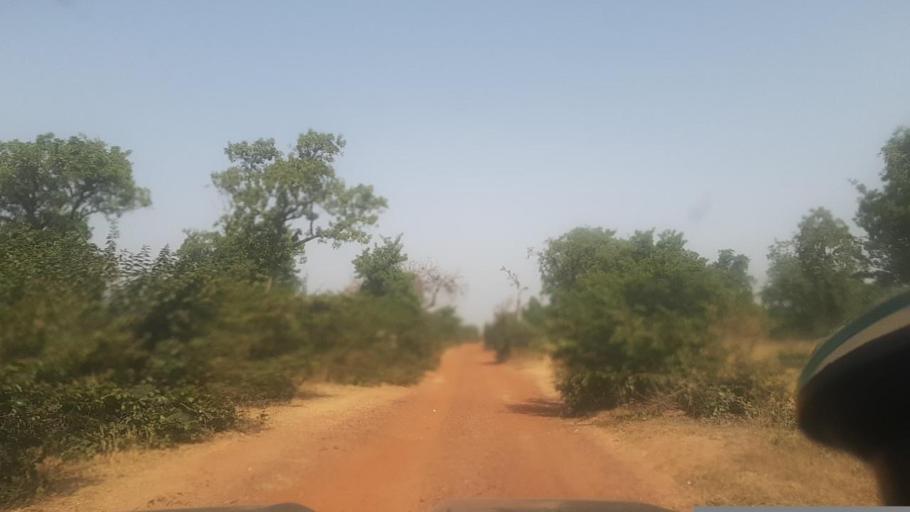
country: ML
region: Segou
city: Bla
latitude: 12.8514
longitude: -5.9848
